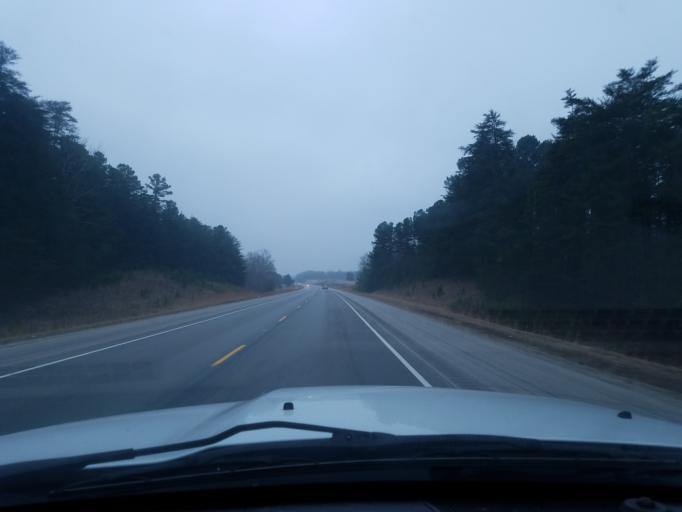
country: US
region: Indiana
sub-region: Perry County
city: Tell City
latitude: 38.1047
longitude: -86.6115
